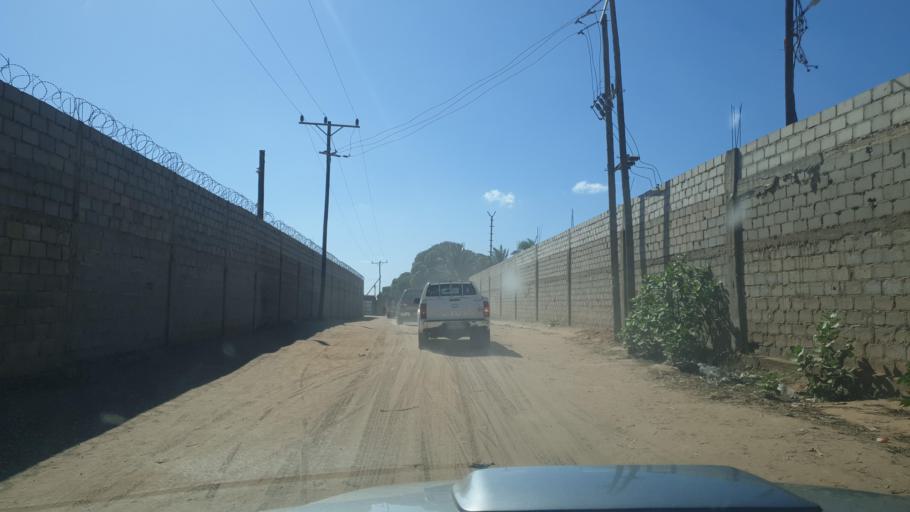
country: MZ
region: Nampula
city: Nacala
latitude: -14.5341
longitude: 40.6980
